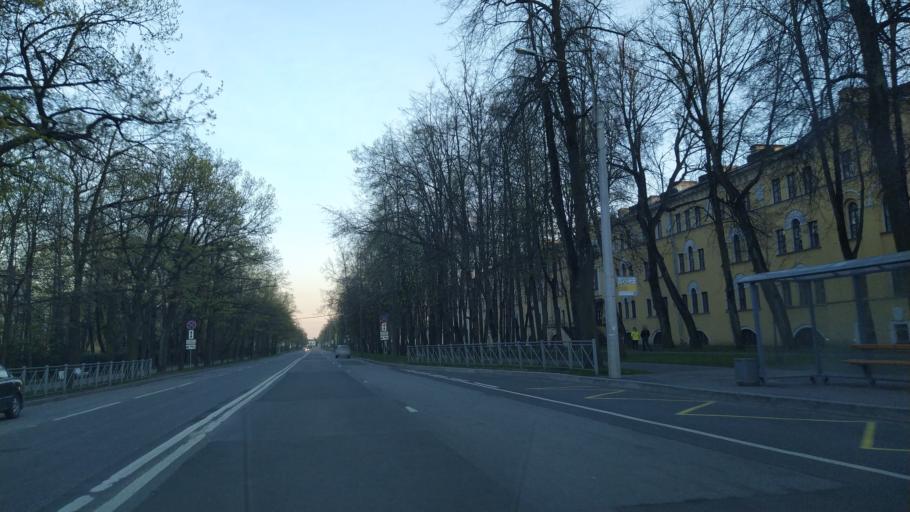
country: RU
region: St.-Petersburg
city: Pushkin
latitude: 59.7100
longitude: 30.4025
